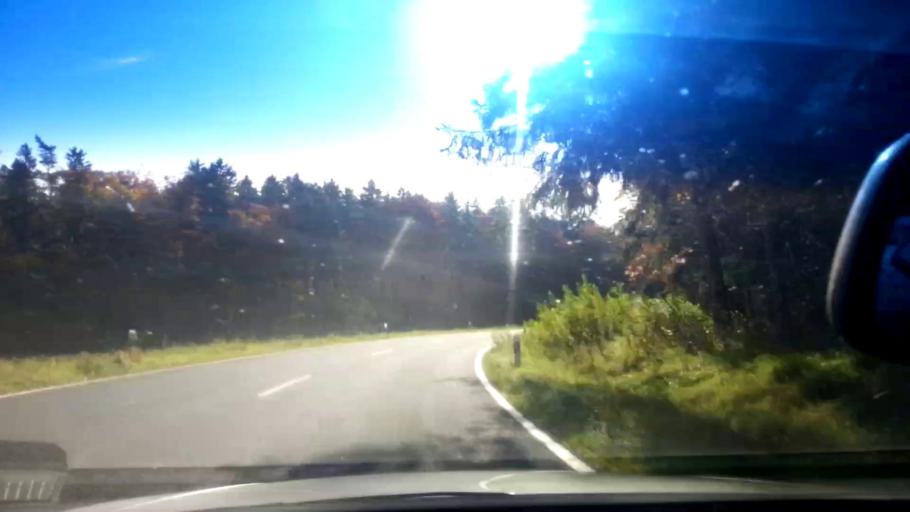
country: DE
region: Bavaria
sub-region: Upper Franconia
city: Poxdorf
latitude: 49.9775
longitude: 11.1278
